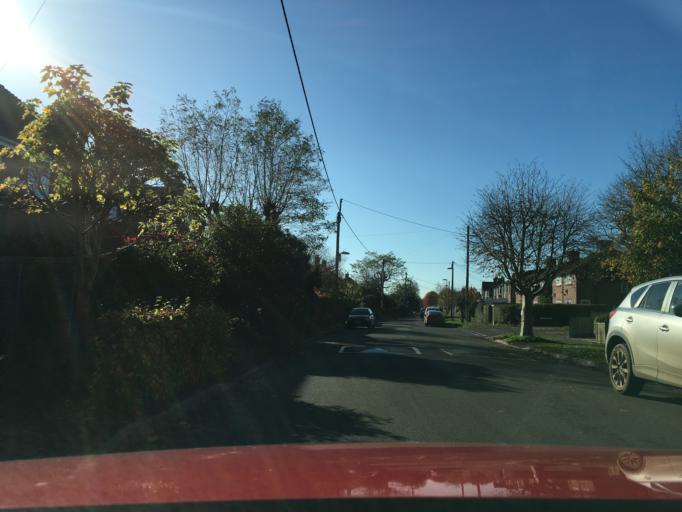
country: GB
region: England
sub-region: Dorset
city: Sherborne
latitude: 50.9405
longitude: -2.5287
